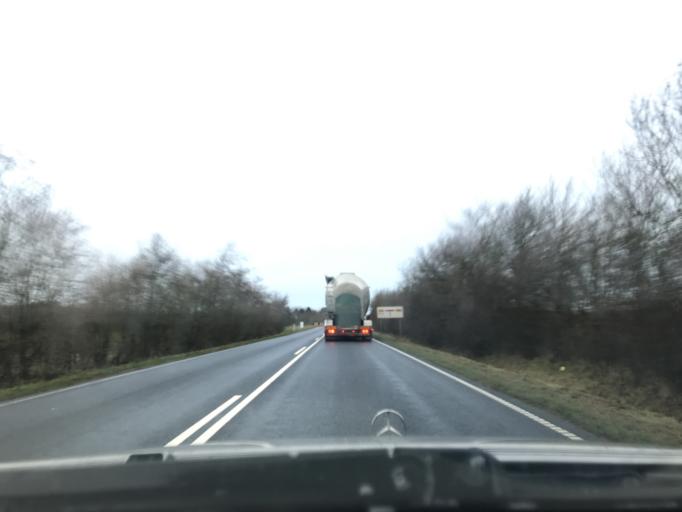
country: DK
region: South Denmark
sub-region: Esbjerg Kommune
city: Ribe
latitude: 55.3107
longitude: 8.7940
